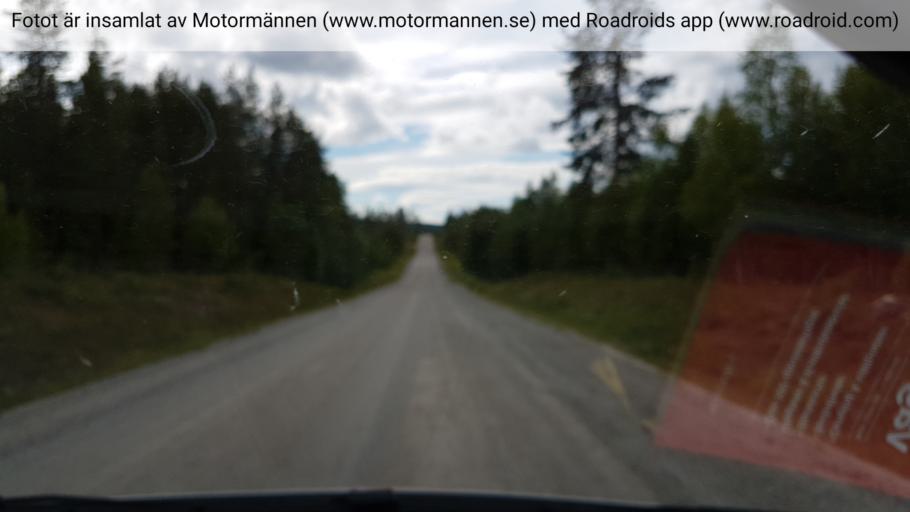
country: SE
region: Vaesternorrland
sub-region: Solleftea Kommun
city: Solleftea
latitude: 63.3449
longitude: 17.4637
